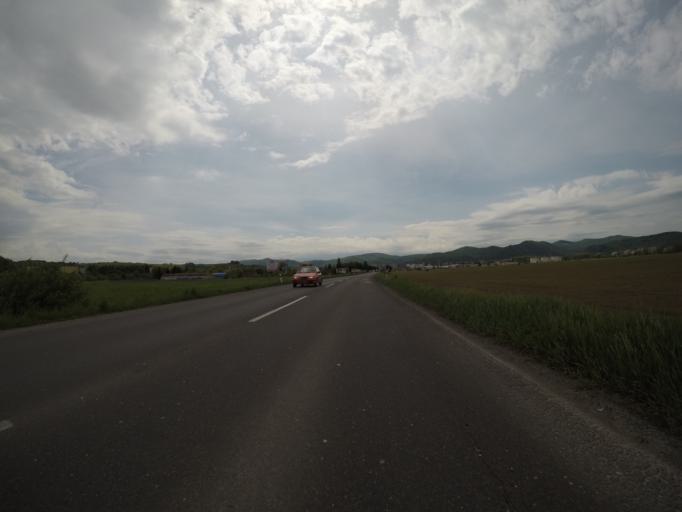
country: SK
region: Banskobystricky
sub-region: Okres Banska Bystrica
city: Zvolen
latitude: 48.5933
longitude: 19.1229
